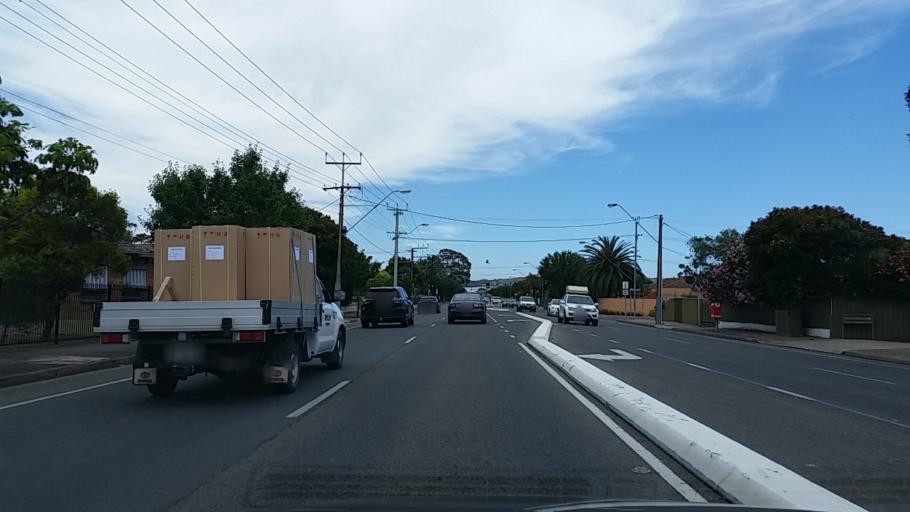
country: AU
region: South Australia
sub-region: Holdfast Bay
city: North Brighton
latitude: -35.0024
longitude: 138.5346
